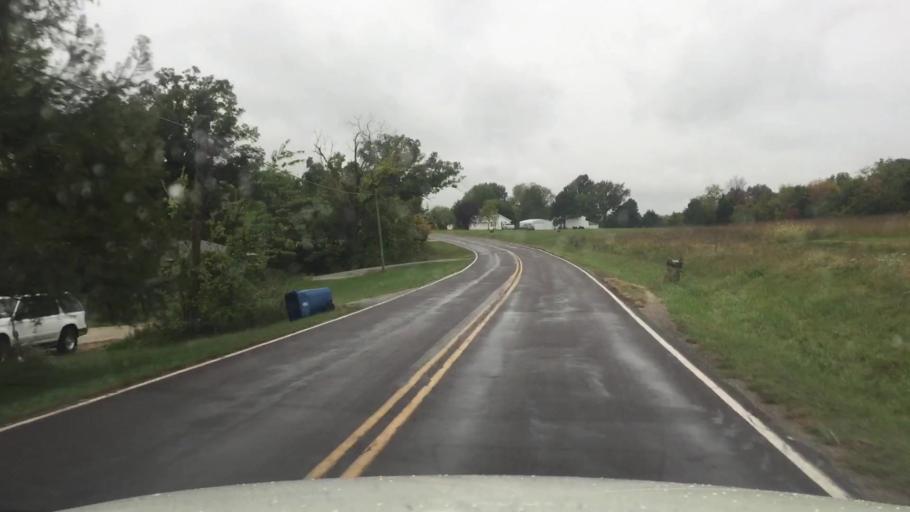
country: US
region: Missouri
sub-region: Boone County
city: Ashland
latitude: 38.7152
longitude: -92.2820
